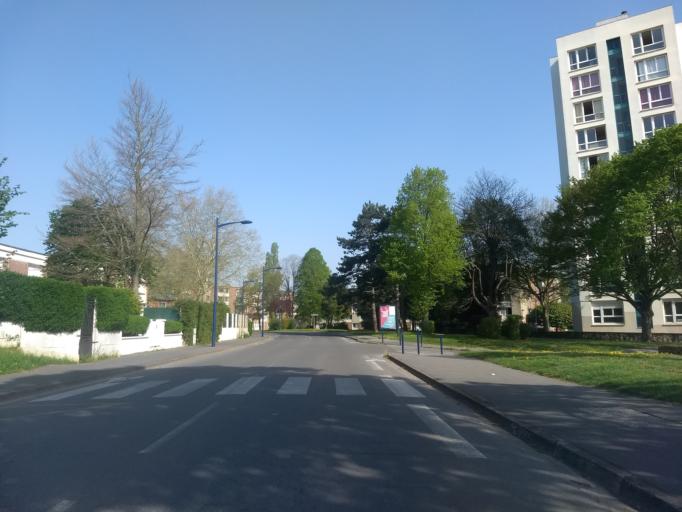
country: FR
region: Nord-Pas-de-Calais
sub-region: Departement du Pas-de-Calais
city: Anzin-Saint-Aubin
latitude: 50.3030
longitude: 2.7459
